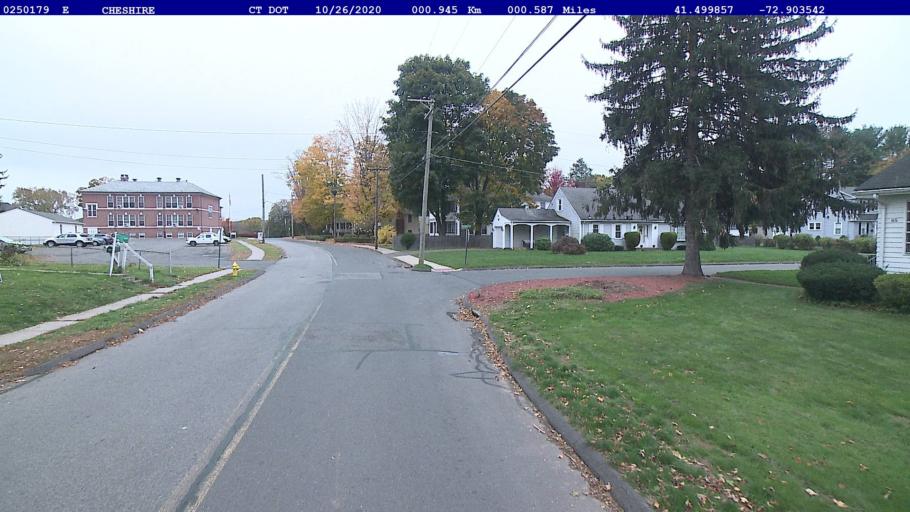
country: US
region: Connecticut
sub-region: New Haven County
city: Cheshire
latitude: 41.4999
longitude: -72.9035
